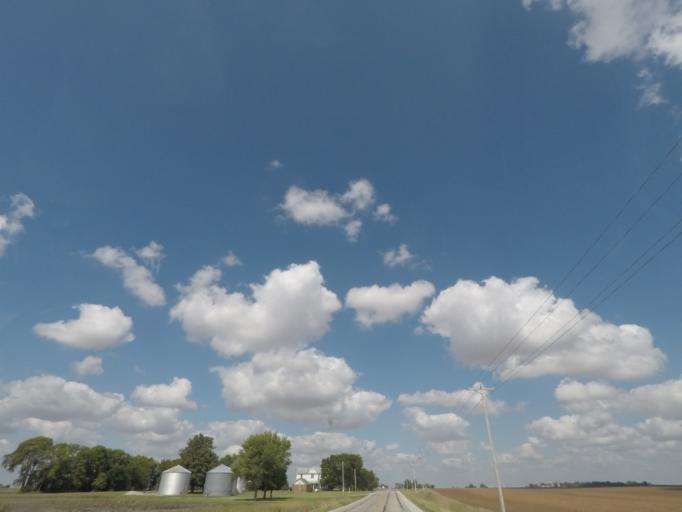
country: US
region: Iowa
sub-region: Story County
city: Nevada
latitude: 42.0520
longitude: -93.4064
